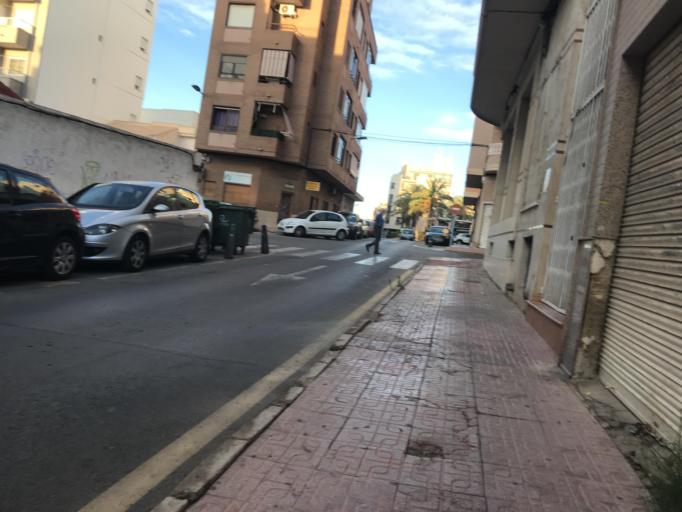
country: ES
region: Valencia
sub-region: Provincia de Alicante
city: Torrevieja
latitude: 37.9800
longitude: -0.6831
